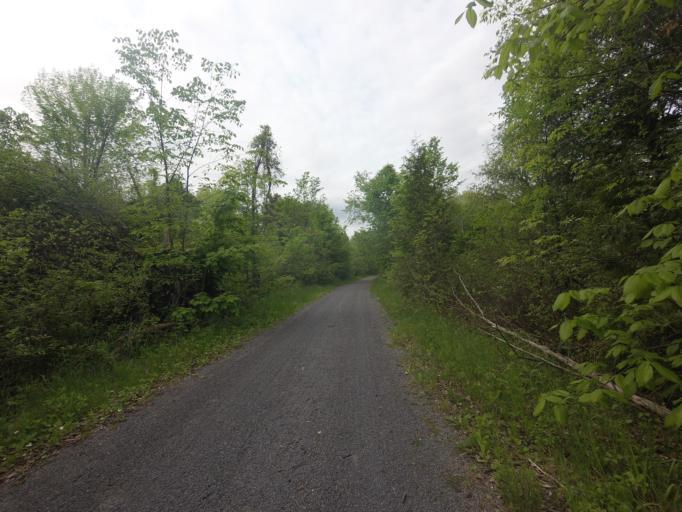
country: CA
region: Ontario
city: Kingston
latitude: 44.3887
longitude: -76.6428
